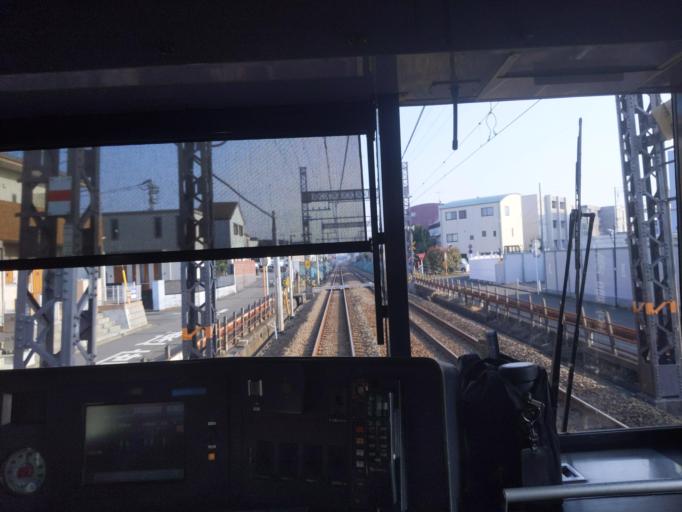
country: JP
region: Kanagawa
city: Fujisawa
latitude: 35.3922
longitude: 139.4679
